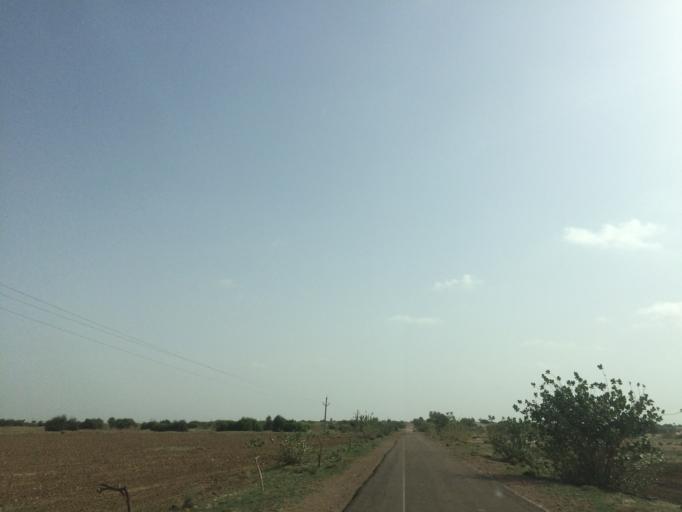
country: IN
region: Rajasthan
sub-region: Jaisalmer
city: Jaisalmer
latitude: 26.8134
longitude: 70.7034
